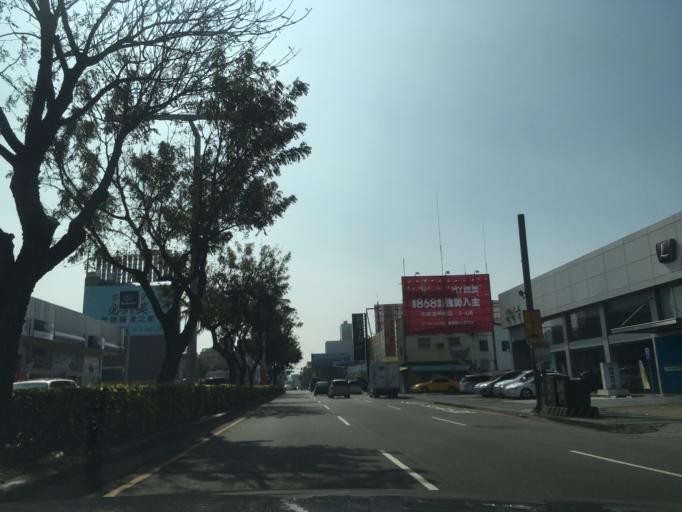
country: TW
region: Taiwan
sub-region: Taichung City
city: Taichung
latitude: 24.1983
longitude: 120.6566
